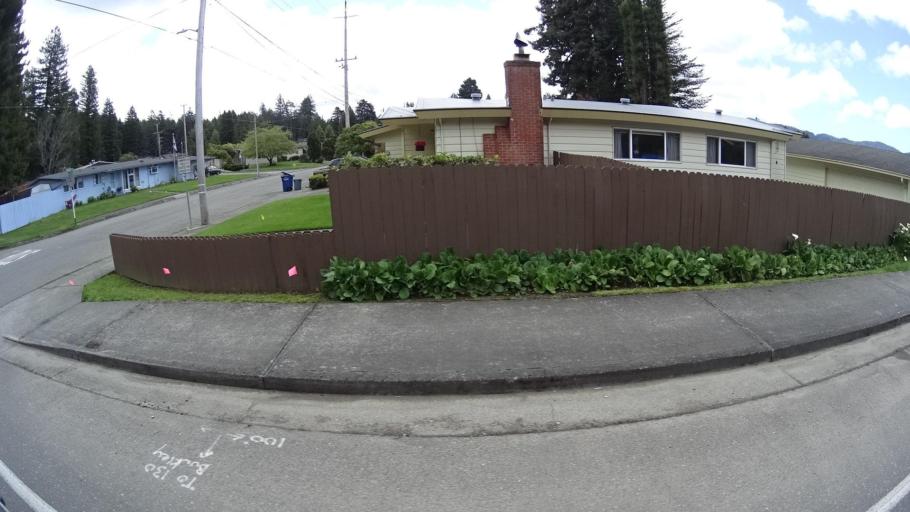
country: US
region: California
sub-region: Humboldt County
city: Blue Lake
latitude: 40.8826
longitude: -123.9807
